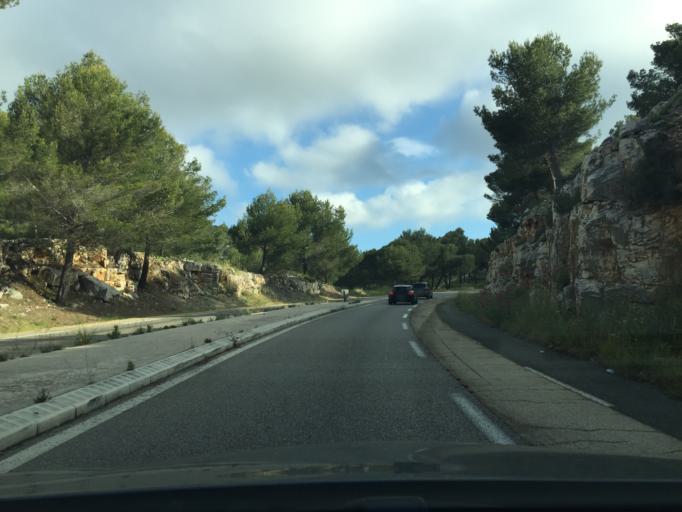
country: FR
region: Provence-Alpes-Cote d'Azur
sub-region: Departement des Bouches-du-Rhone
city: Cassis
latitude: 43.2349
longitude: 5.5433
